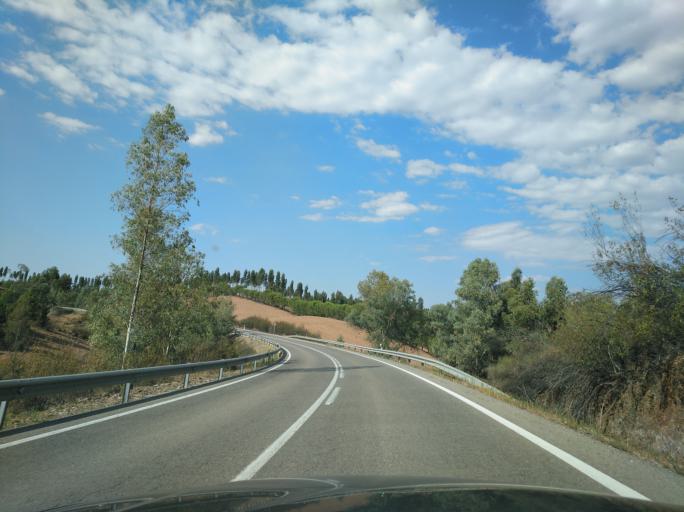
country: ES
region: Andalusia
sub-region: Provincia de Huelva
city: Santa Barbara de Casa
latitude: 37.8559
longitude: -7.2092
